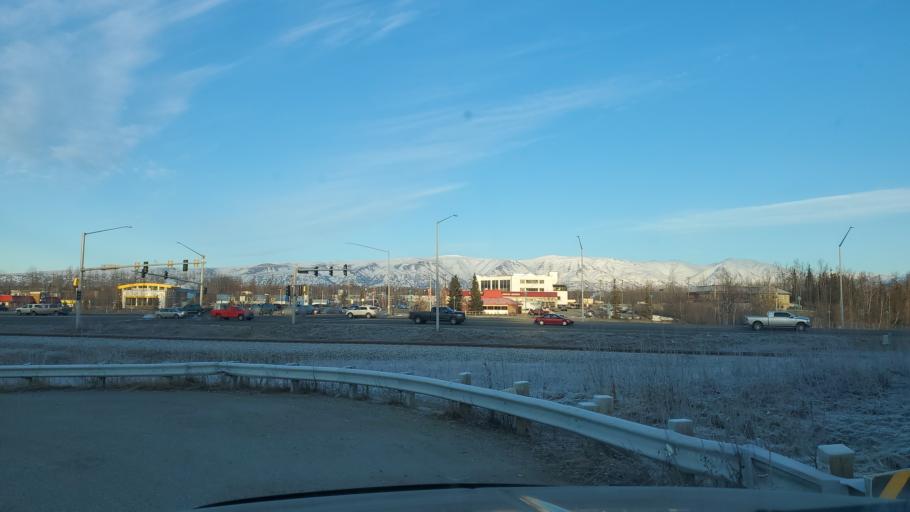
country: US
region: Alaska
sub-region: Matanuska-Susitna Borough
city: Wasilla
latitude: 61.5796
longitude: -149.4293
